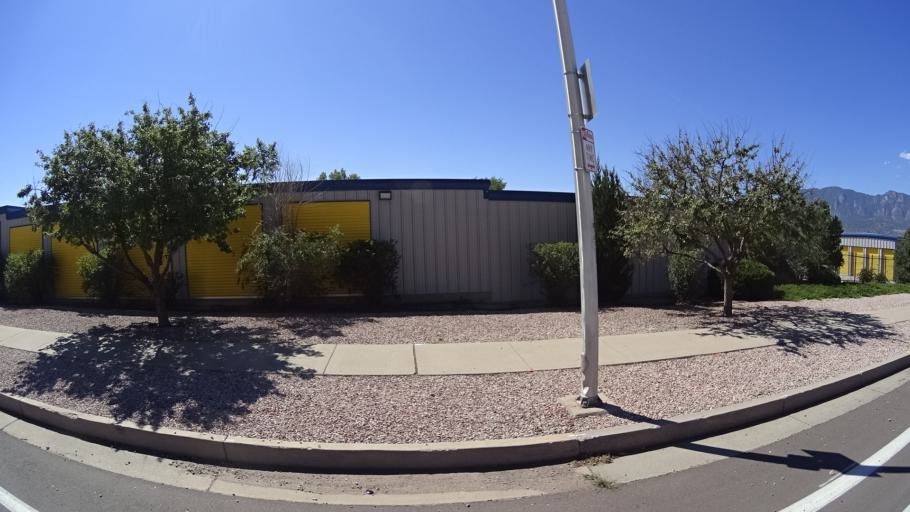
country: US
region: Colorado
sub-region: El Paso County
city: Stratmoor
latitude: 38.7872
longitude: -104.7608
